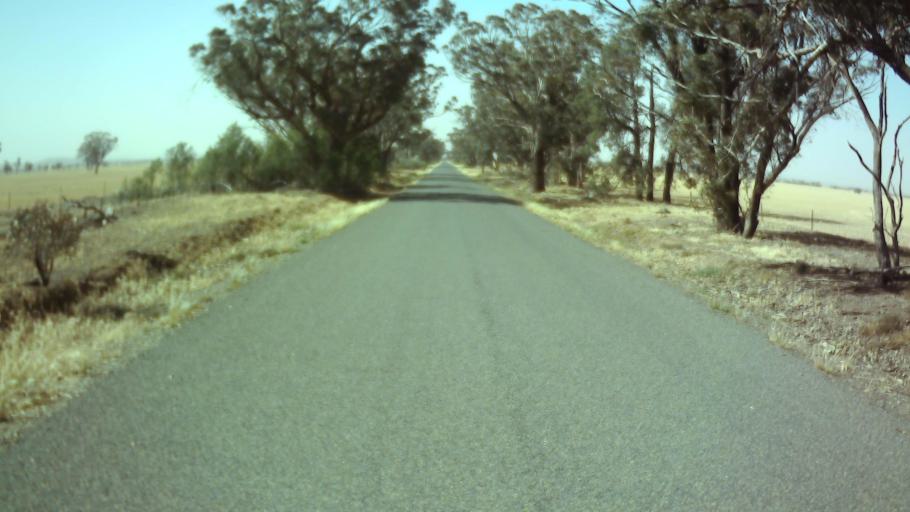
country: AU
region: New South Wales
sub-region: Weddin
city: Grenfell
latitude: -33.8920
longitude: 147.9223
